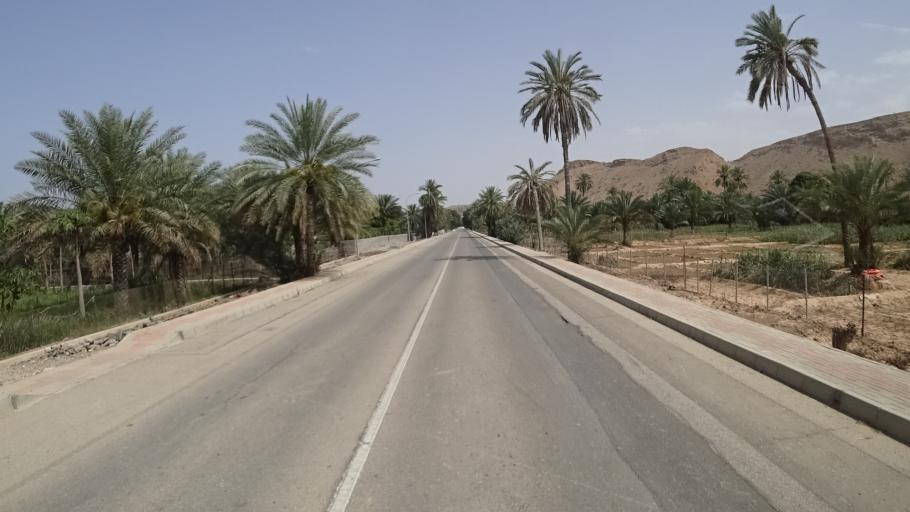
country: OM
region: Muhafazat Masqat
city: Muscat
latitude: 23.1713
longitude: 58.9154
